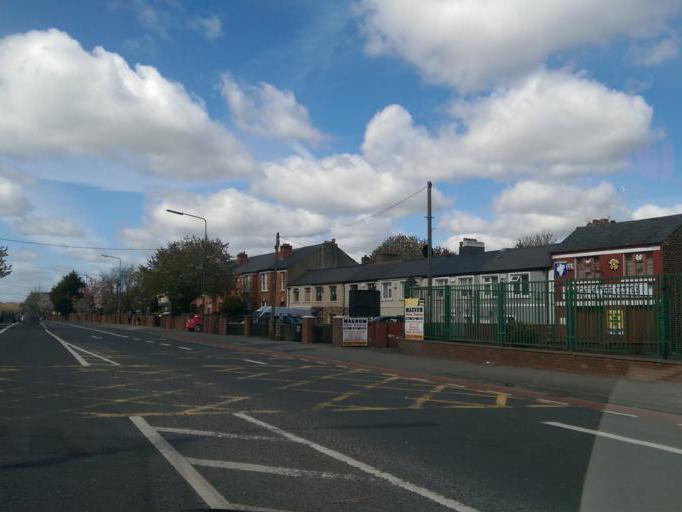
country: IE
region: Leinster
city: Crumlin
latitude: 53.3248
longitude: -6.3215
